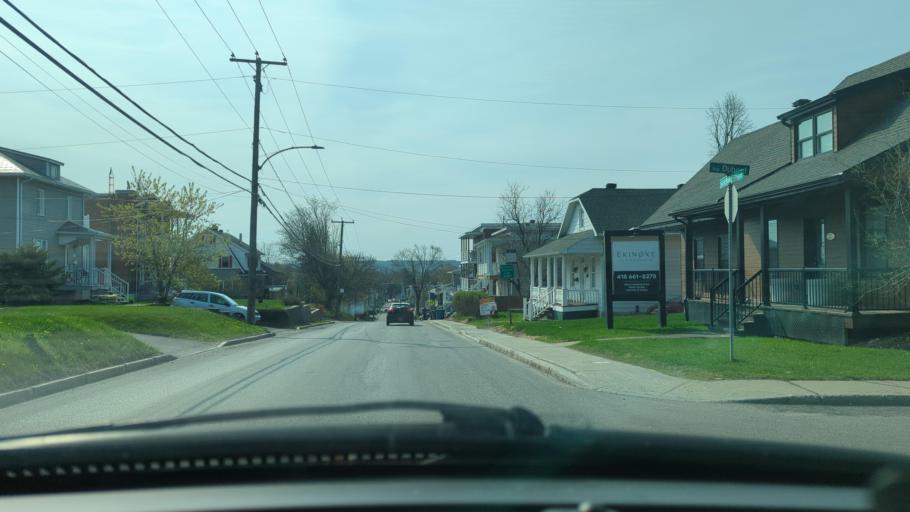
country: CA
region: Quebec
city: Quebec
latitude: 46.8534
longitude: -71.2136
